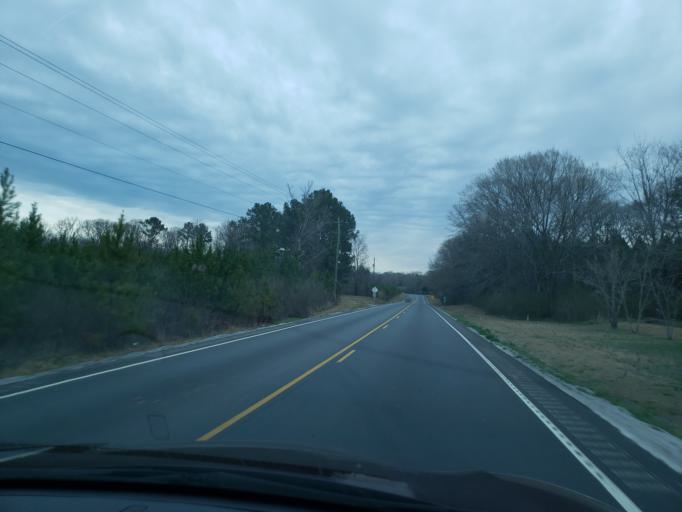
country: US
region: Alabama
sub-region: Randolph County
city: Roanoke
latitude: 33.0493
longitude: -85.3334
